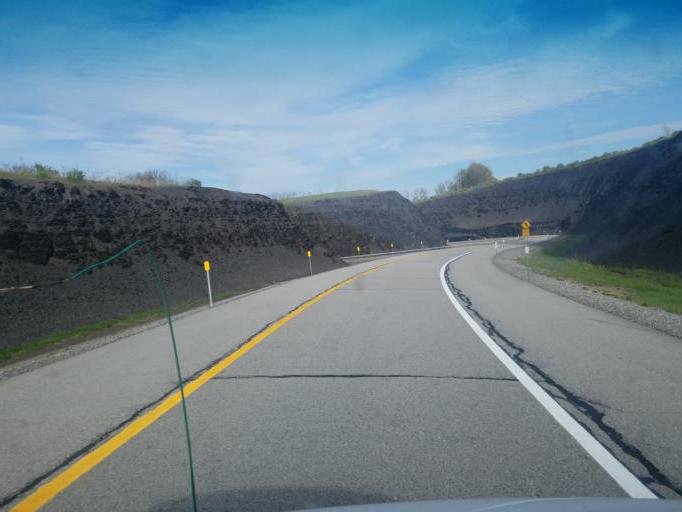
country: US
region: New York
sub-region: Herkimer County
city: Little Falls
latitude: 43.0156
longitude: -74.8212
